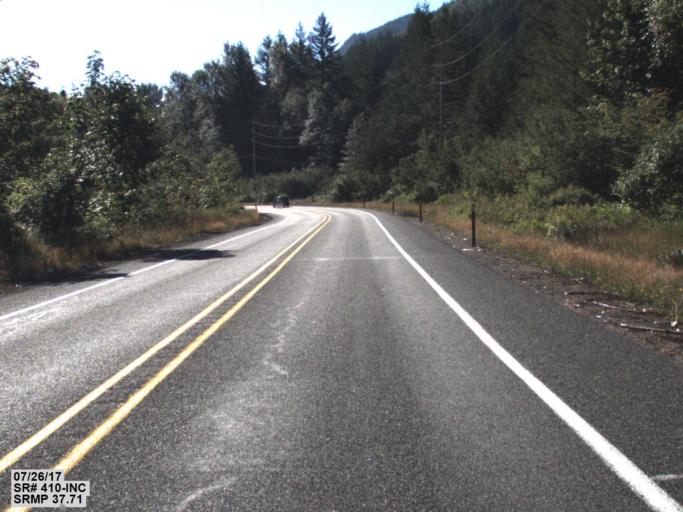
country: US
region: Washington
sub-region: King County
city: Enumclaw
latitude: 47.1655
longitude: -121.7558
